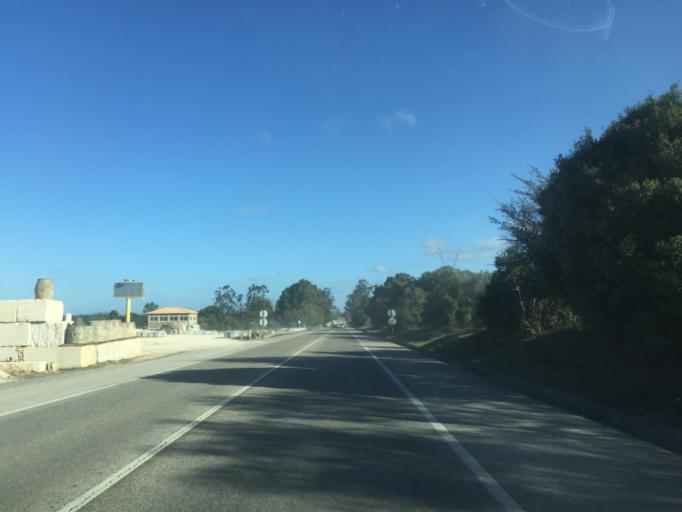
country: PT
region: Leiria
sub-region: Alcobaca
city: Turquel
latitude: 39.4558
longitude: -8.9474
